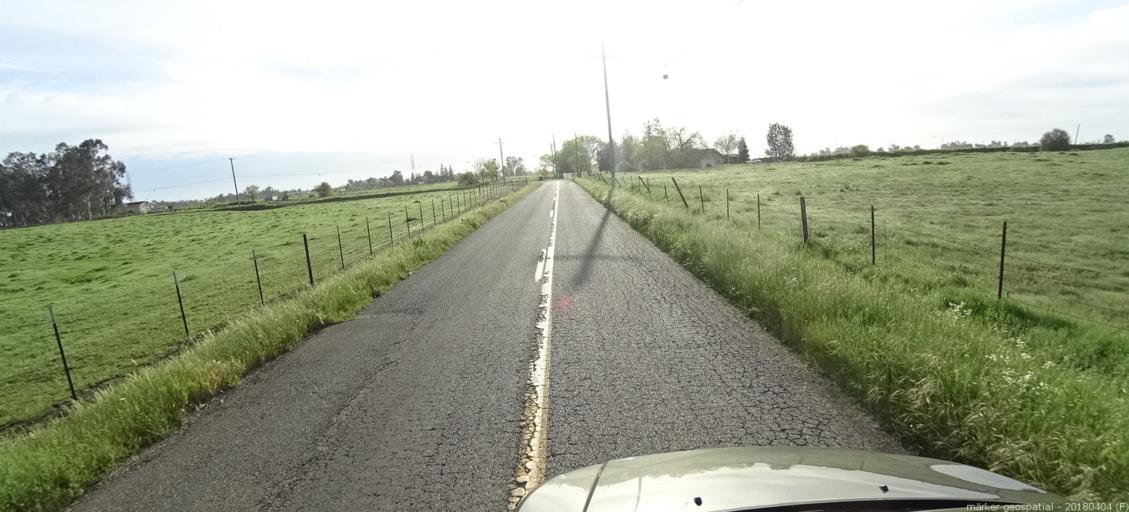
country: US
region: California
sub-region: Sacramento County
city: Herald
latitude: 38.3360
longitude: -121.2554
